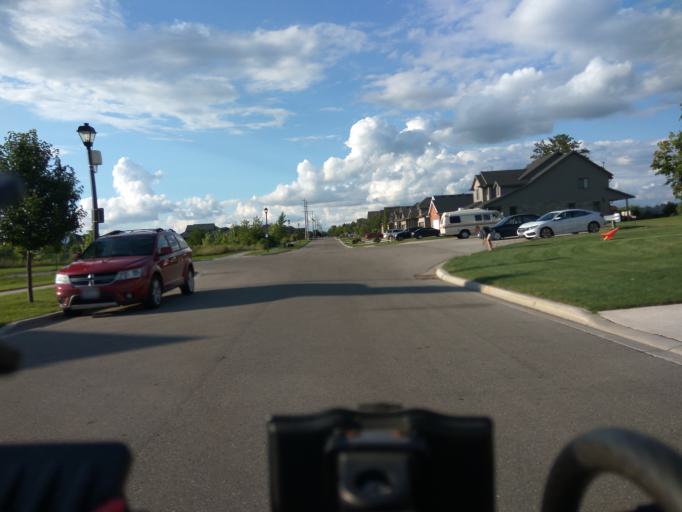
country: CA
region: Ontario
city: Stratford
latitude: 43.3841
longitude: -80.9585
